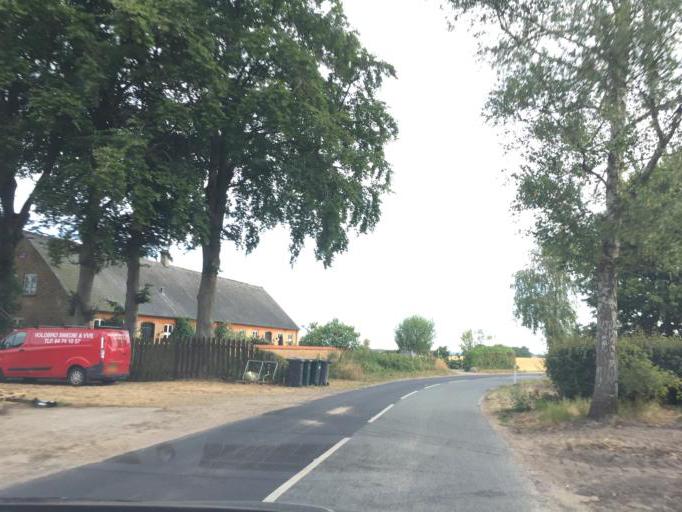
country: DK
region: South Denmark
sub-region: Assens Kommune
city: Assens
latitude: 55.2743
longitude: 9.9767
